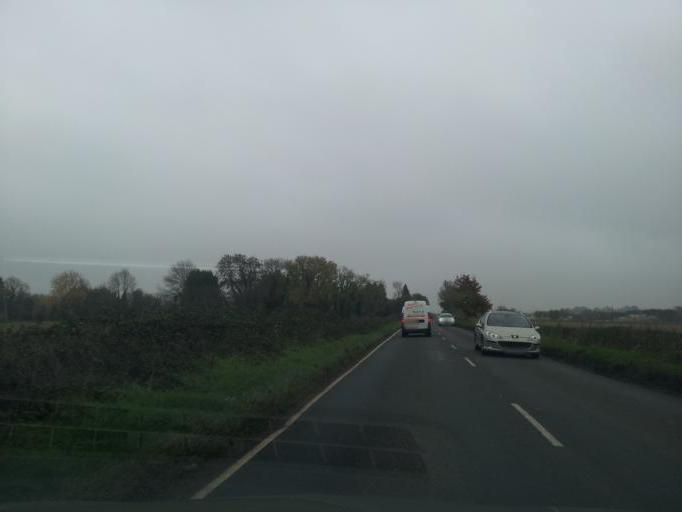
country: GB
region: England
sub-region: Northamptonshire
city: Brackley
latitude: 52.0208
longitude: -1.1017
